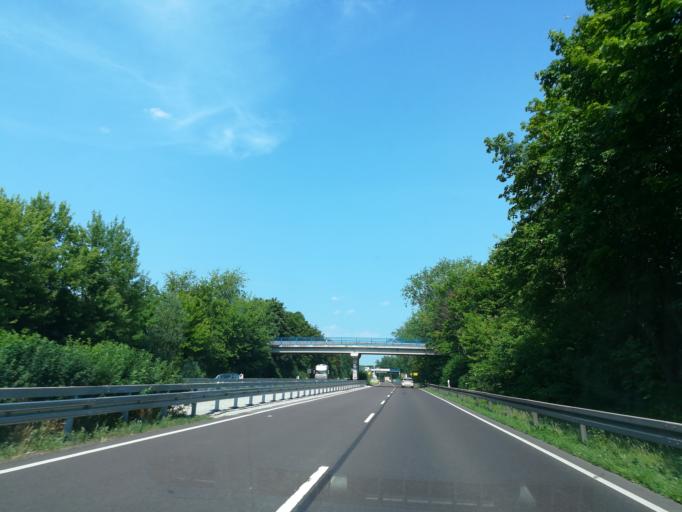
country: DE
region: Saxony-Anhalt
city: Diesdorf
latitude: 52.0803
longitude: 11.5857
